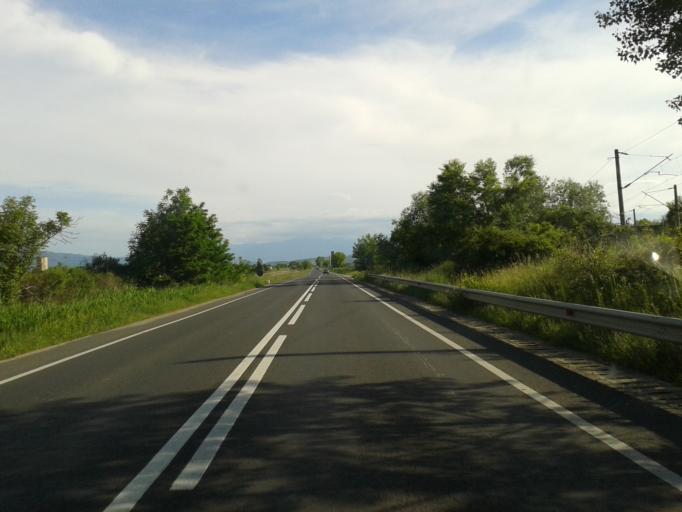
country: RO
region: Hunedoara
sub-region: Comuna Calan
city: Calan
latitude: 45.7494
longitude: 23.0009
